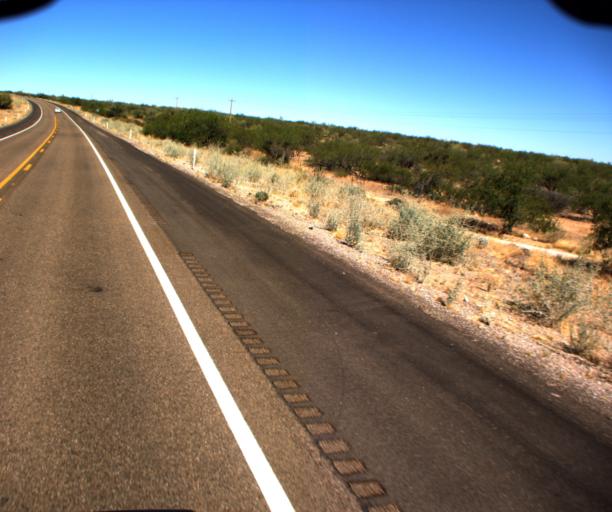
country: US
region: Arizona
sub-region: Pima County
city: Three Points
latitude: 32.0363
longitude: -111.5379
